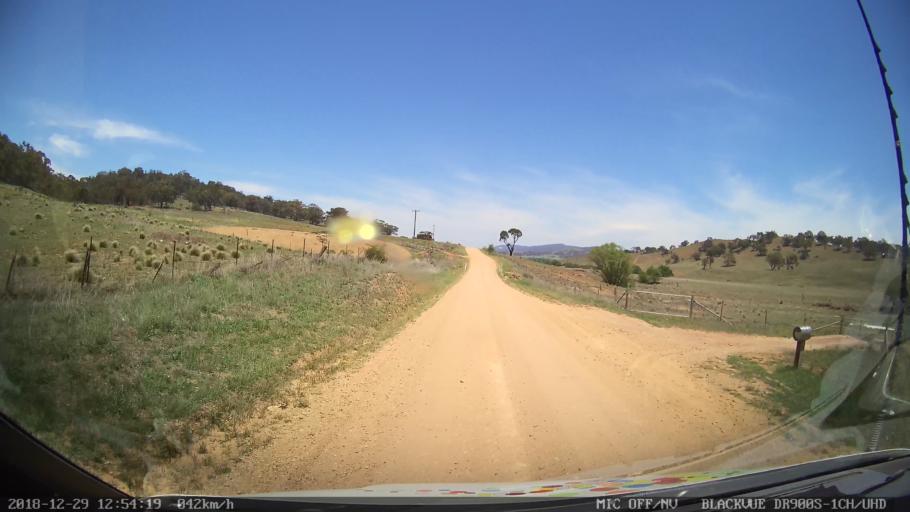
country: AU
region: Australian Capital Territory
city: Macarthur
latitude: -35.6905
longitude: 149.1875
